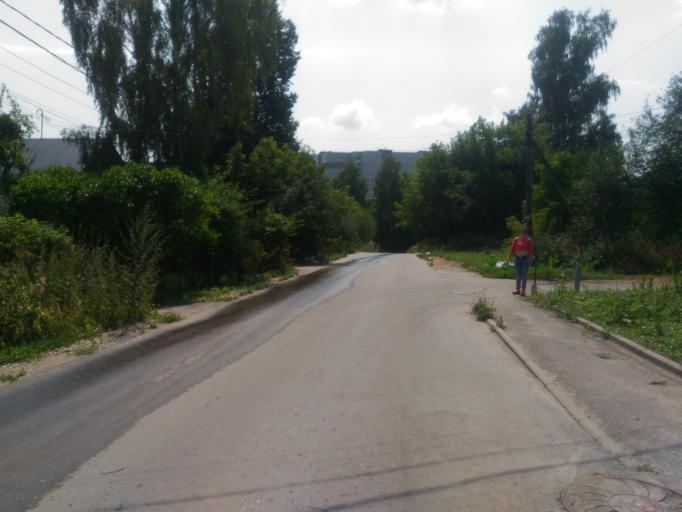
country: RU
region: Tula
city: Mendeleyevskiy
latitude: 54.1627
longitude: 37.6083
